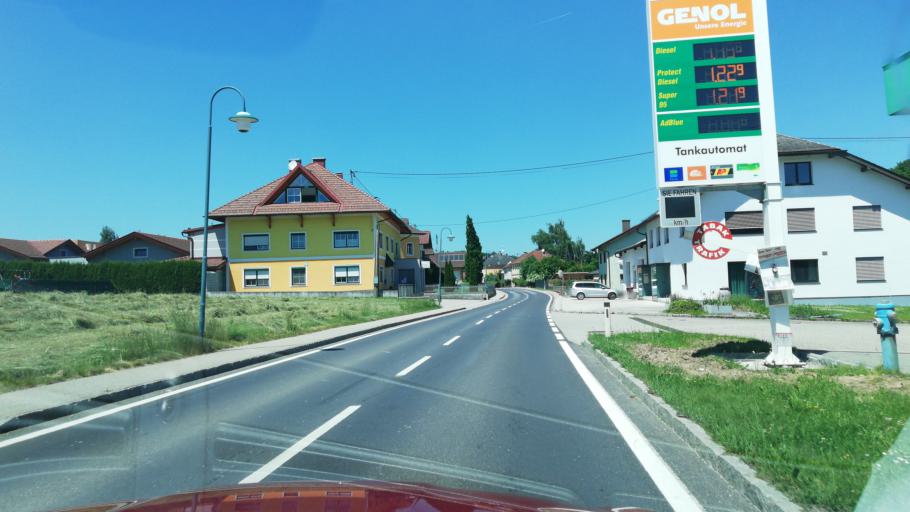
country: AT
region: Upper Austria
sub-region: Wels-Land
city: Aichkirchen
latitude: 48.0967
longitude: 13.7711
